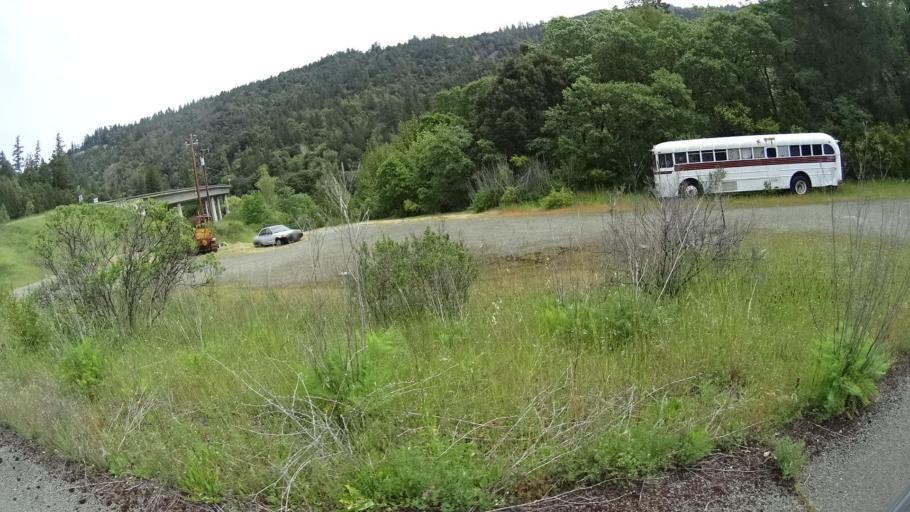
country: US
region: California
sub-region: Humboldt County
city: Redway
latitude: 40.0308
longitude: -123.7801
